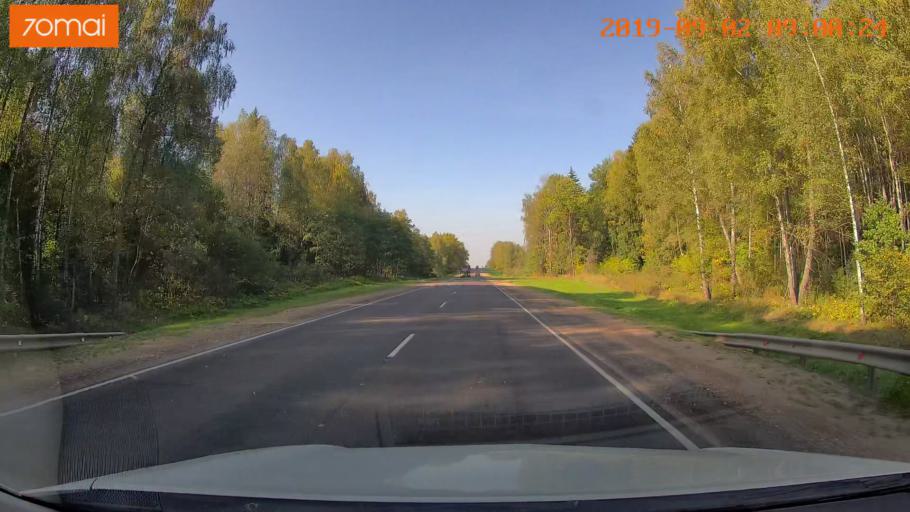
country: RU
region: Kaluga
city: Myatlevo
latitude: 54.9130
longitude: 35.7077
